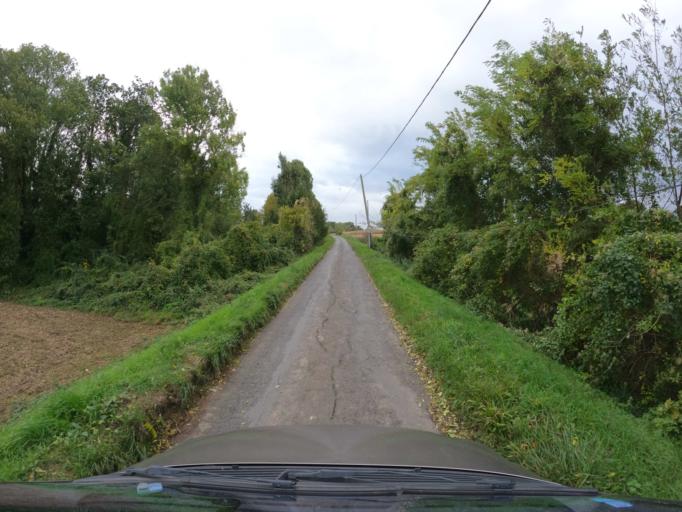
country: FR
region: Ile-de-France
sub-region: Departement de Seine-et-Marne
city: Montry
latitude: 48.8756
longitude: 2.8261
